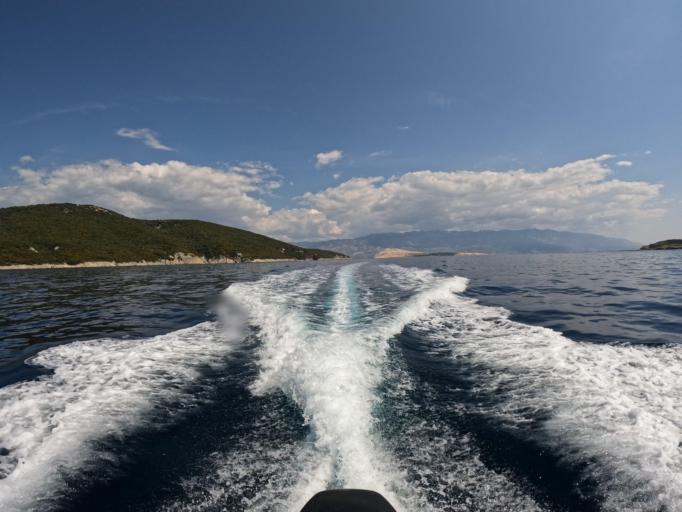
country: HR
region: Primorsko-Goranska
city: Lopar
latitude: 44.8550
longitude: 14.7471
